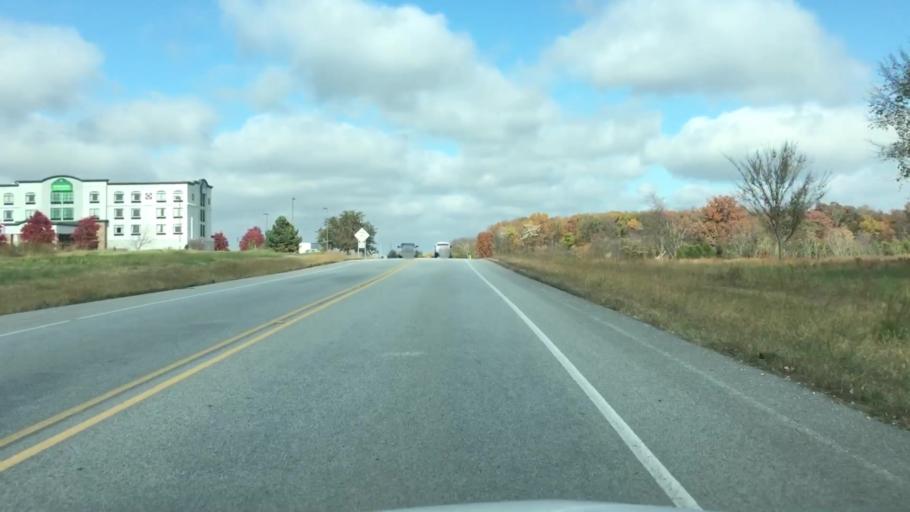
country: US
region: Arkansas
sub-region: Benton County
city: Centerton
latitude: 36.3015
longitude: -94.3039
